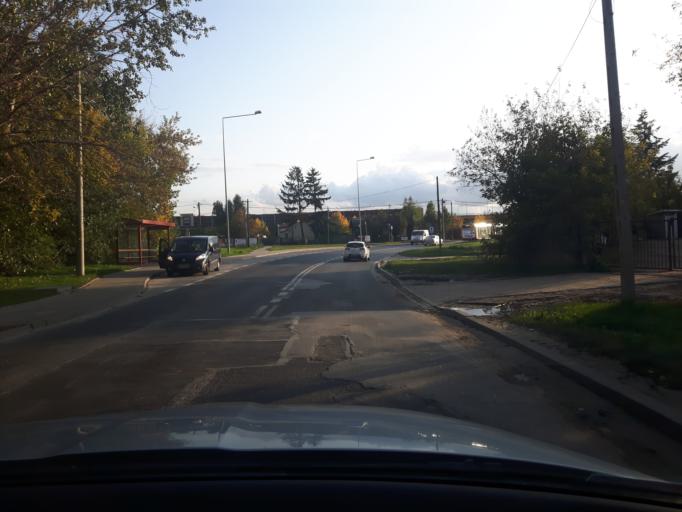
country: PL
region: Masovian Voivodeship
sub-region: Warszawa
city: Wlochy
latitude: 52.1583
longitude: 20.9922
